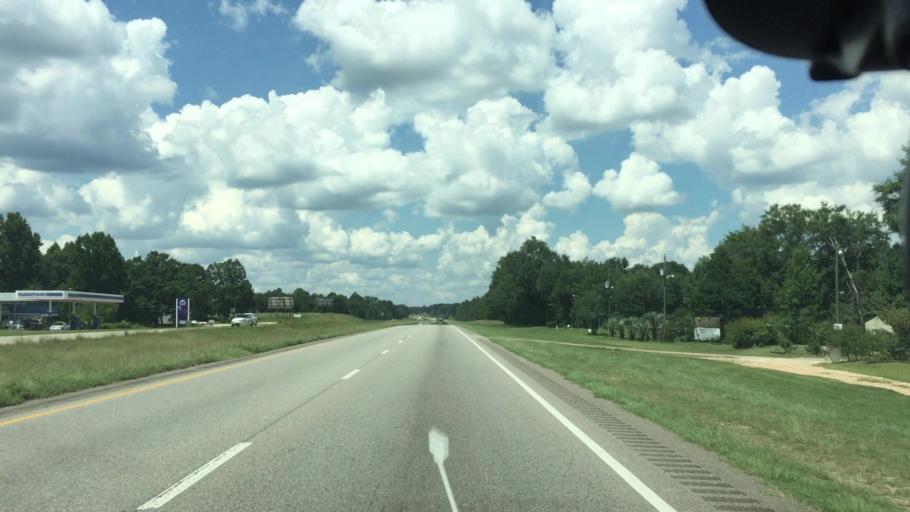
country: US
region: Alabama
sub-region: Pike County
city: Troy
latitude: 31.8548
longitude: -85.9966
